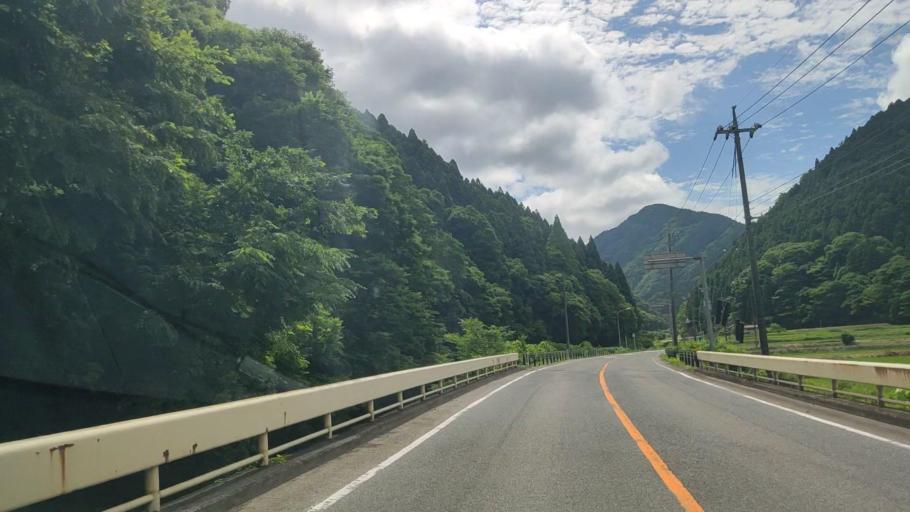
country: JP
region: Okayama
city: Niimi
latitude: 35.2166
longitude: 133.4596
